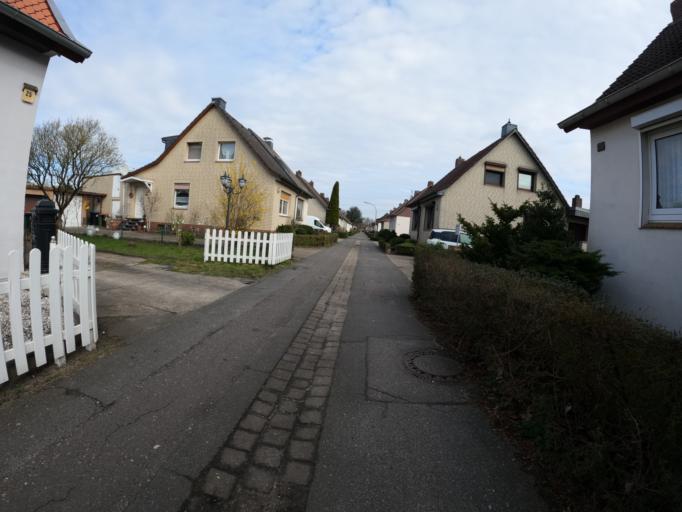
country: DE
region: Hamburg
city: Harburg
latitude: 53.4733
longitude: 9.9269
